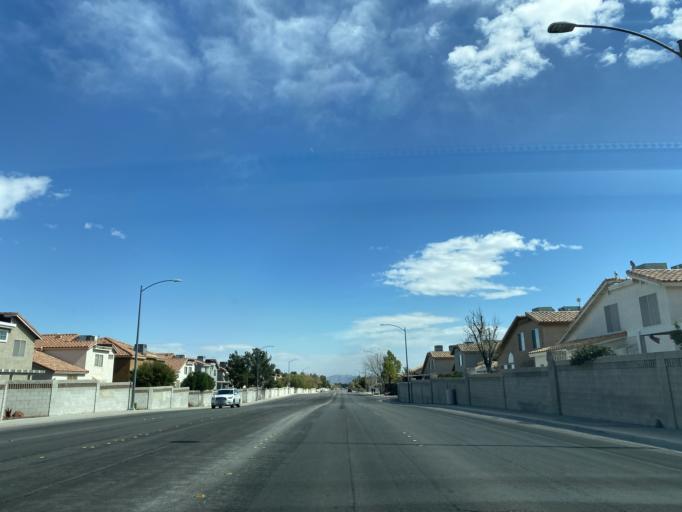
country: US
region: Nevada
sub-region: Clark County
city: Summerlin South
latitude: 36.2262
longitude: -115.2875
